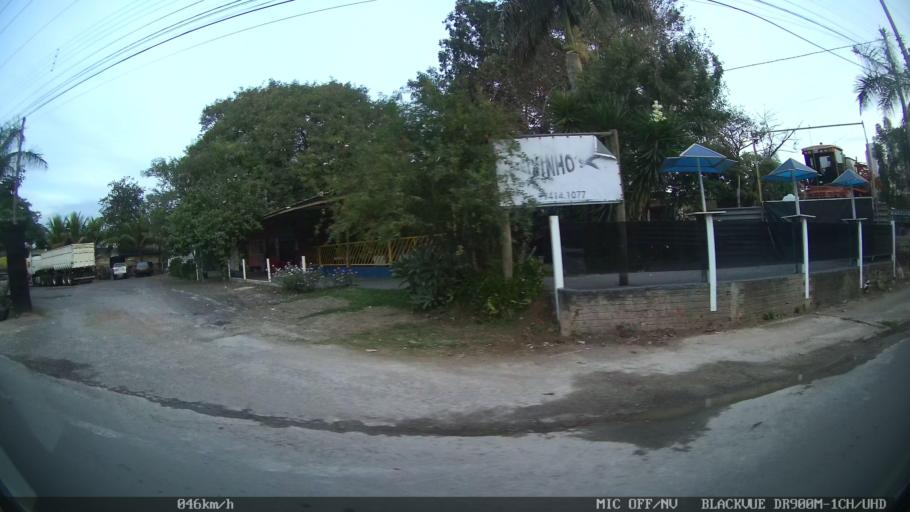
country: BR
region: Sao Paulo
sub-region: Limeira
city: Limeira
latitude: -22.5449
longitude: -47.4154
